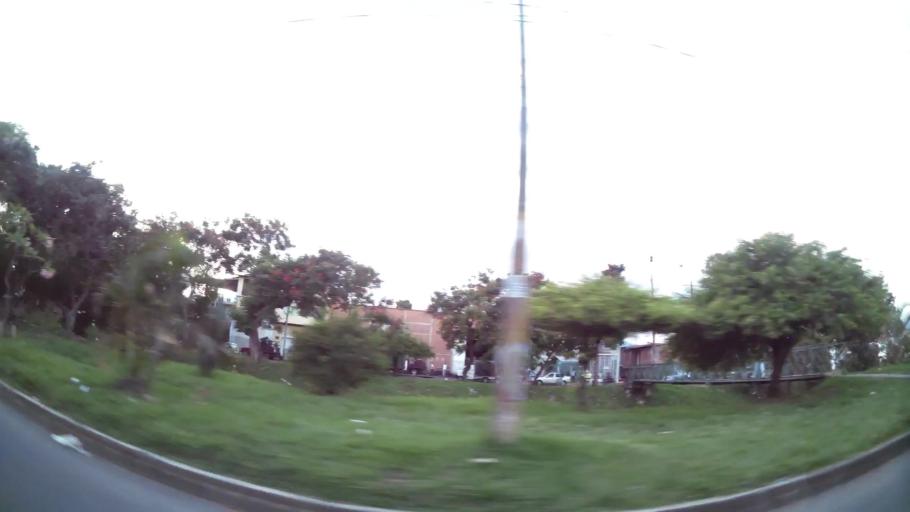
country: CO
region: Valle del Cauca
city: Cali
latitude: 3.4316
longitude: -76.4836
